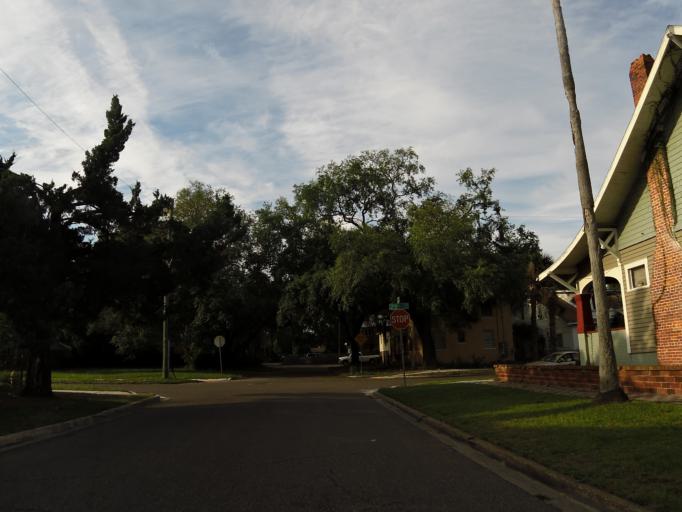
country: US
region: Florida
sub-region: Duval County
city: Jacksonville
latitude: 30.3582
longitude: -81.6554
